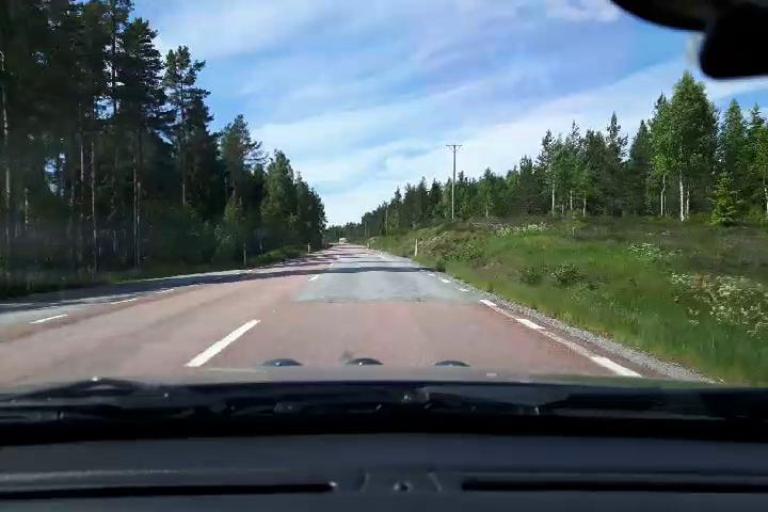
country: SE
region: Gaevleborg
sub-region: Soderhamns Kommun
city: Soderhamn
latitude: 61.1280
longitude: 16.9285
